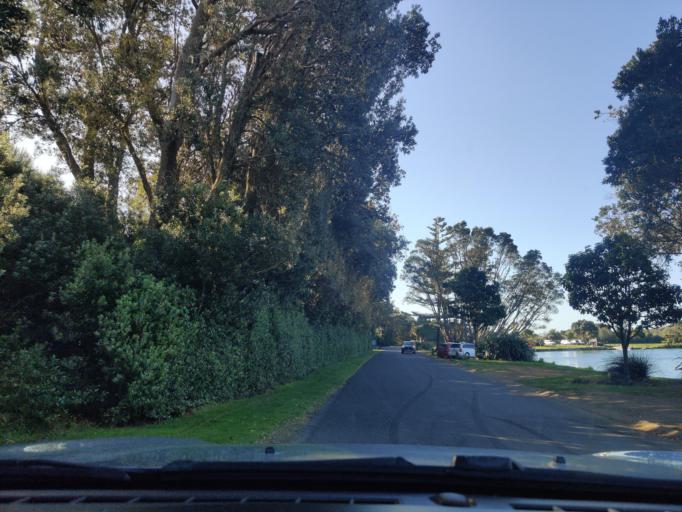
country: NZ
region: Taranaki
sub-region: New Plymouth District
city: New Plymouth
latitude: -39.0423
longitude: 174.1128
